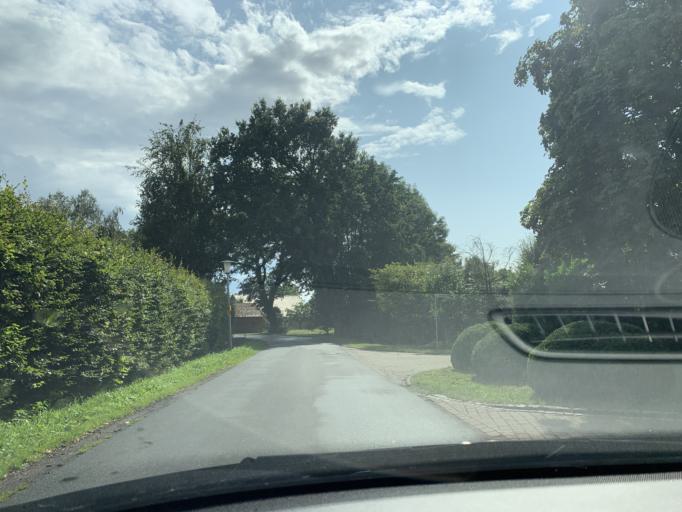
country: DE
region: Lower Saxony
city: Westerstede
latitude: 53.2727
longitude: 7.9001
